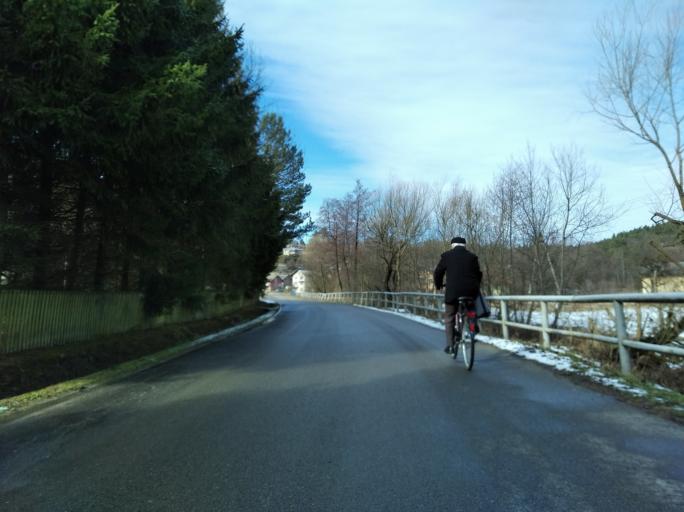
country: PL
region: Subcarpathian Voivodeship
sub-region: Powiat brzozowski
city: Jasienica Rosielna
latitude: 49.7547
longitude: 21.9099
